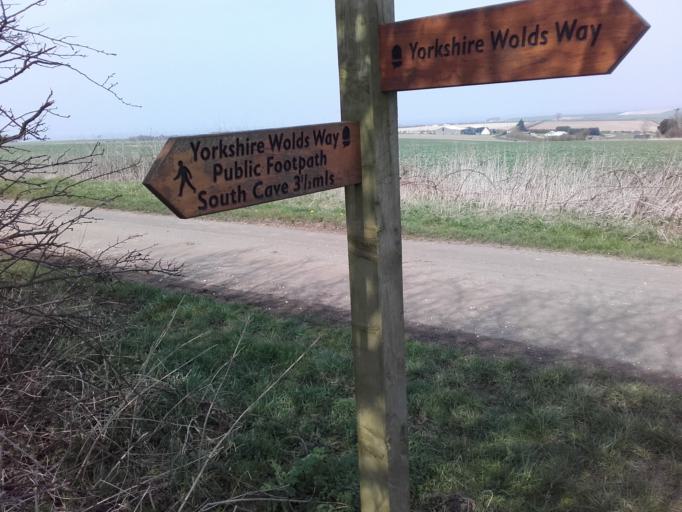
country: GB
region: England
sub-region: East Riding of Yorkshire
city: South Cave
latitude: 53.8050
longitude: -0.5742
